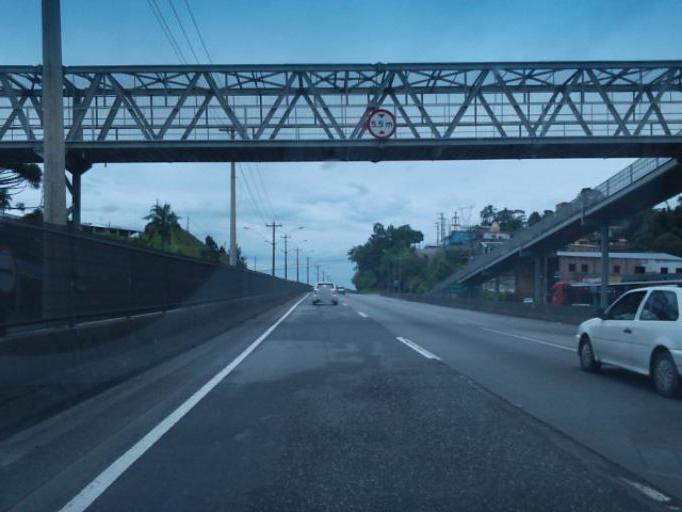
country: BR
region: Sao Paulo
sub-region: Sao Lourenco Da Serra
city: Sao Lourenco da Serra
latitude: -23.8853
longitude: -46.9759
